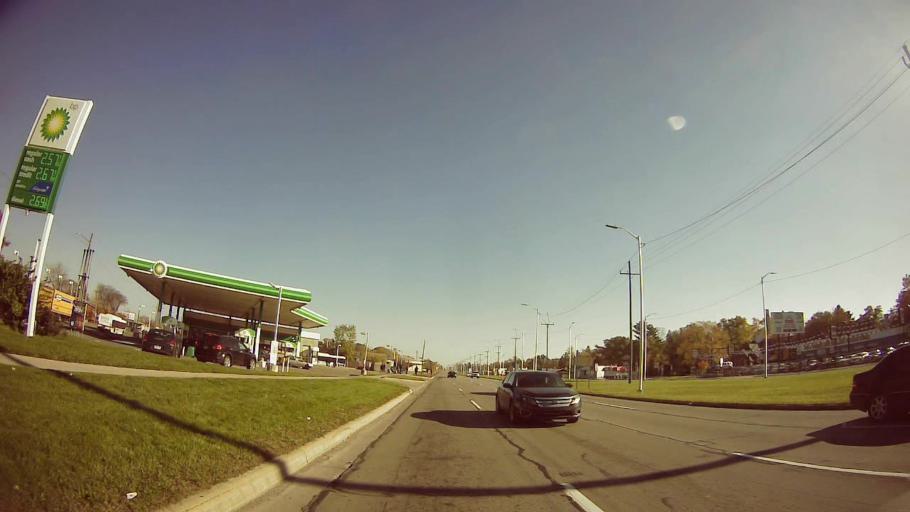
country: US
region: Michigan
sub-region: Wayne County
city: Redford
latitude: 42.4284
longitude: -83.2867
